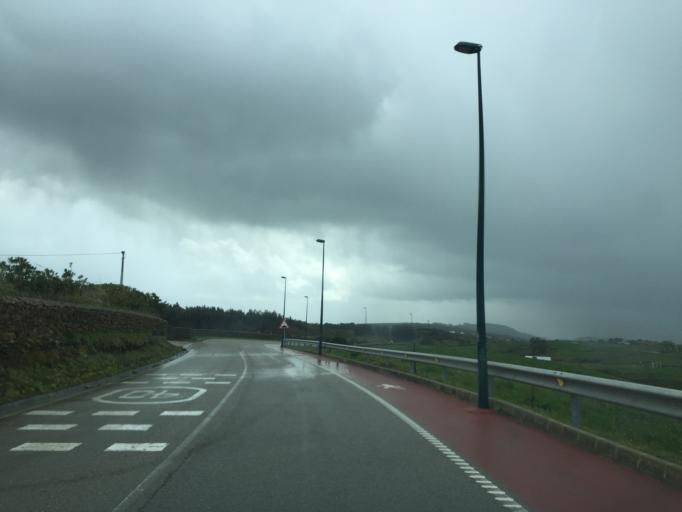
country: ES
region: Cantabria
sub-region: Provincia de Cantabria
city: Suances
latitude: 43.4319
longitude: -4.0581
